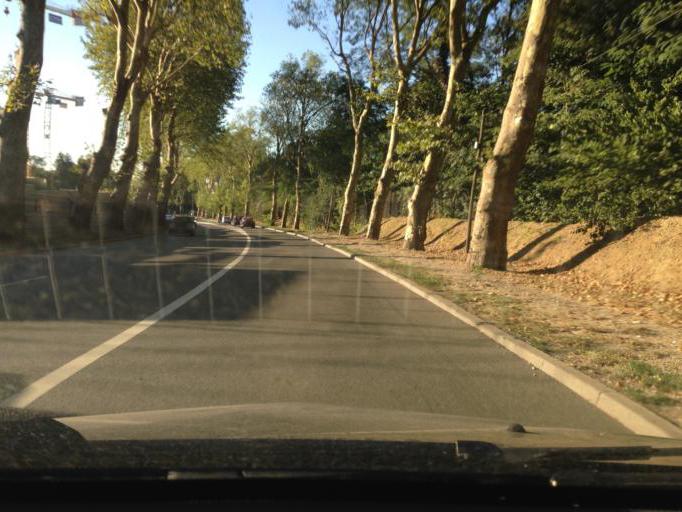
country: FR
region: Ile-de-France
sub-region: Departement des Yvelines
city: Louveciennes
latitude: 48.8689
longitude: 2.1129
